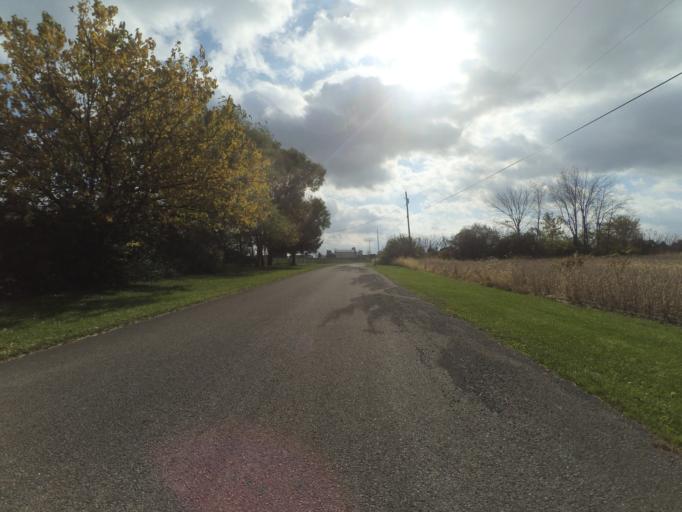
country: US
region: Pennsylvania
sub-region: Centre County
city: Bellefonte
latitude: 40.8899
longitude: -77.8145
